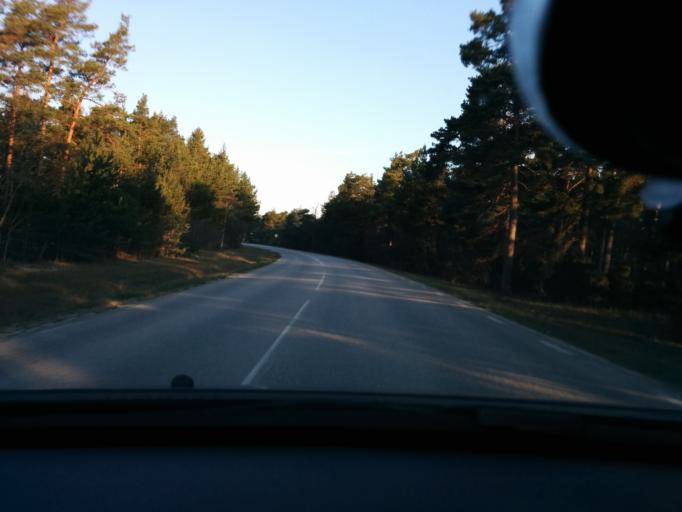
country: SE
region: Gotland
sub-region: Gotland
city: Visby
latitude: 57.6372
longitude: 18.4008
